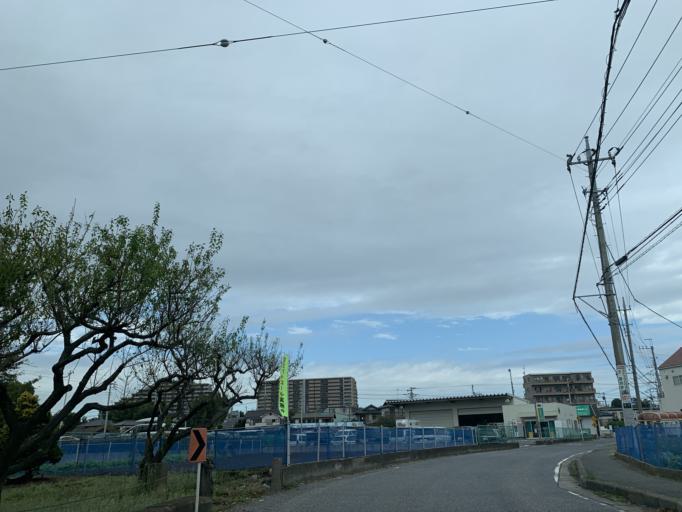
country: JP
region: Chiba
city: Kashiwa
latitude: 35.8742
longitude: 139.9507
